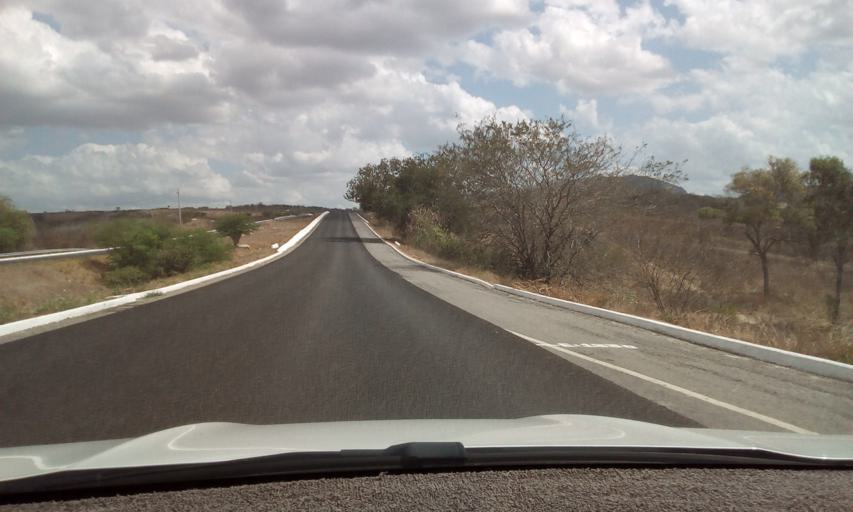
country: BR
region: Pernambuco
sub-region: Toritama
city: Toritama
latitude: -8.0576
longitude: -36.0484
